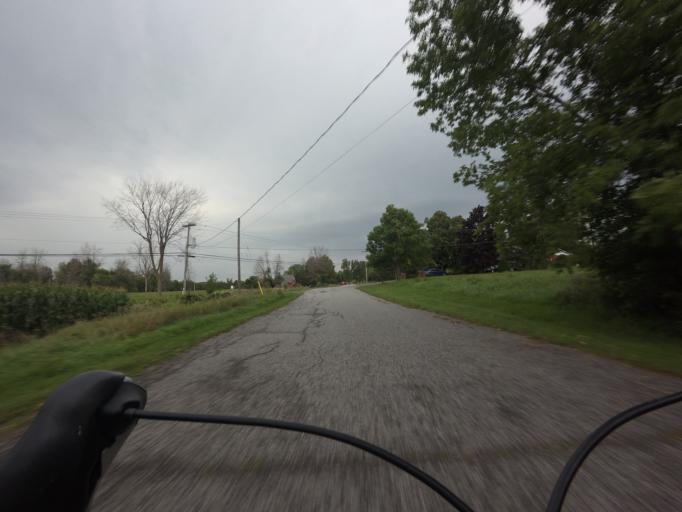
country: CA
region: Ontario
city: Bells Corners
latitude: 45.1577
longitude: -75.7069
